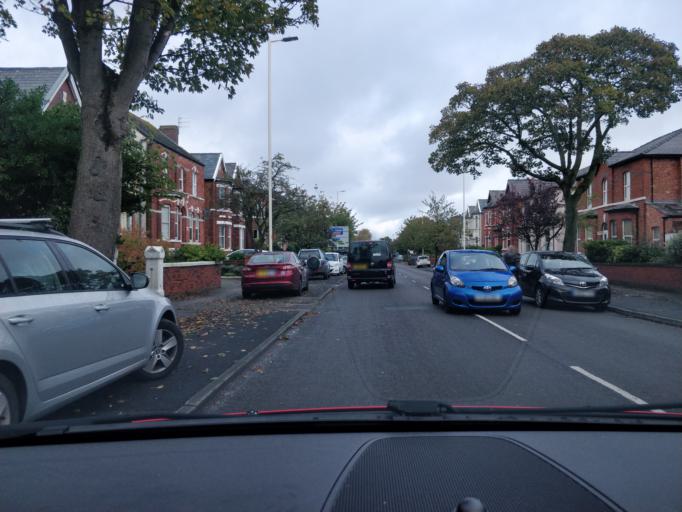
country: GB
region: England
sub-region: Sefton
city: Southport
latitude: 53.6283
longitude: -3.0119
